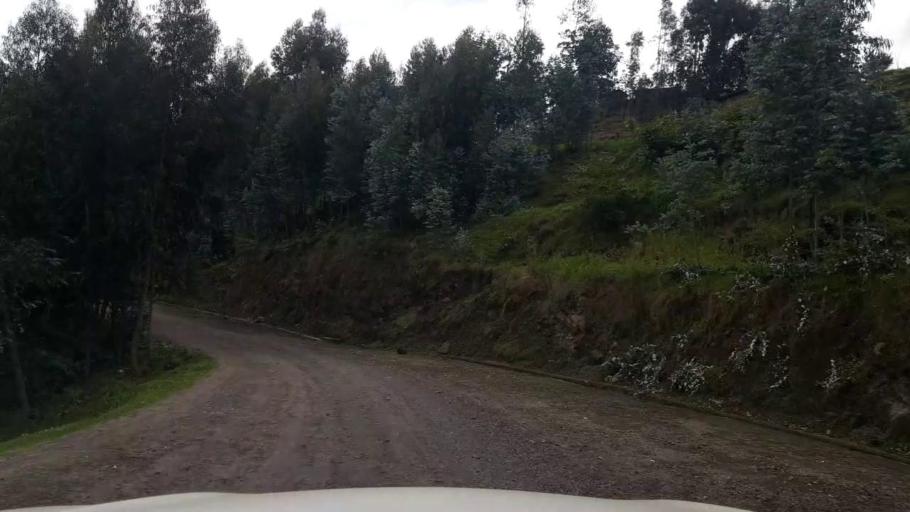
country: RW
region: Northern Province
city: Musanze
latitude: -1.5200
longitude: 29.5335
